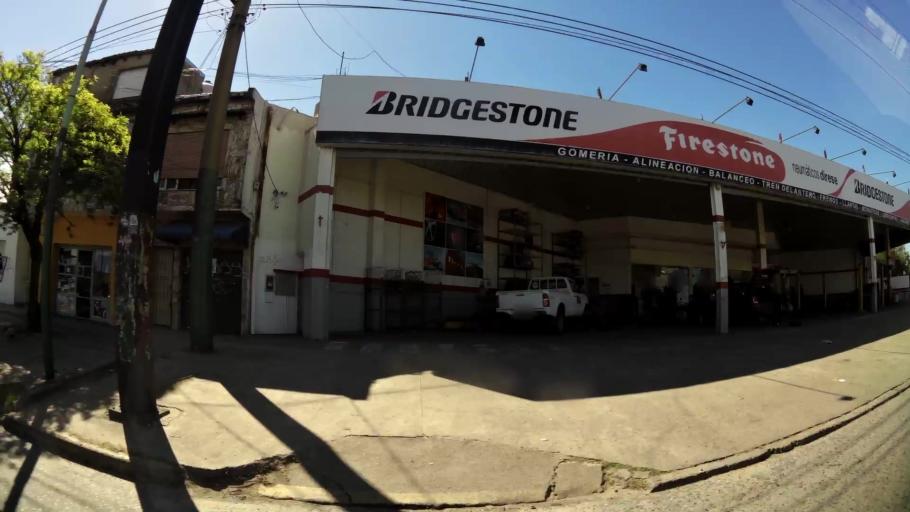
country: AR
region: Buenos Aires
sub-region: Partido de Almirante Brown
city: Adrogue
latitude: -34.7960
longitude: -58.3648
